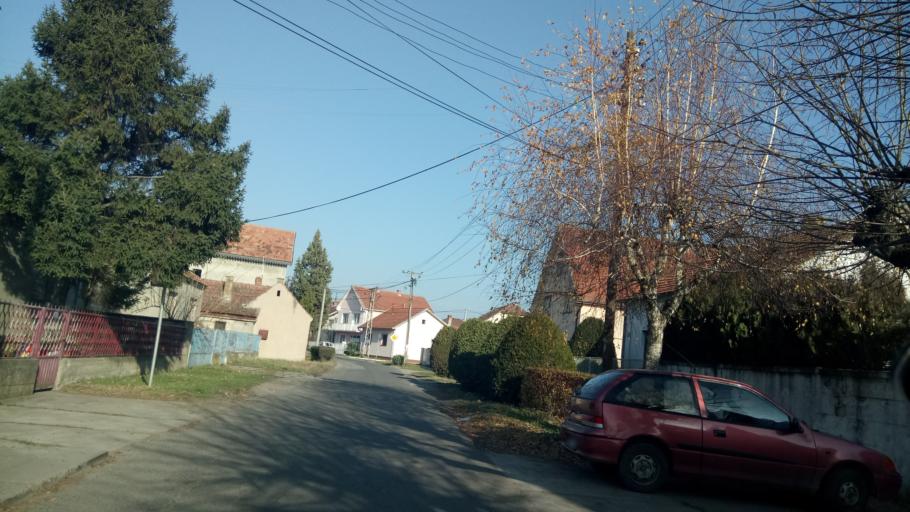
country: RS
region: Autonomna Pokrajina Vojvodina
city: Nova Pazova
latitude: 44.9433
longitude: 20.2109
